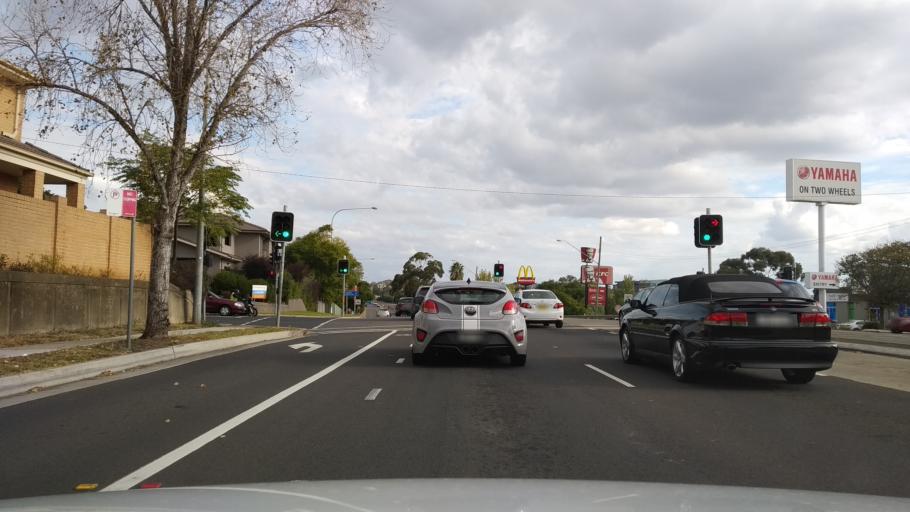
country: AU
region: New South Wales
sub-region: Campbelltown Municipality
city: Campbelltown
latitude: -34.0706
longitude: 150.8121
